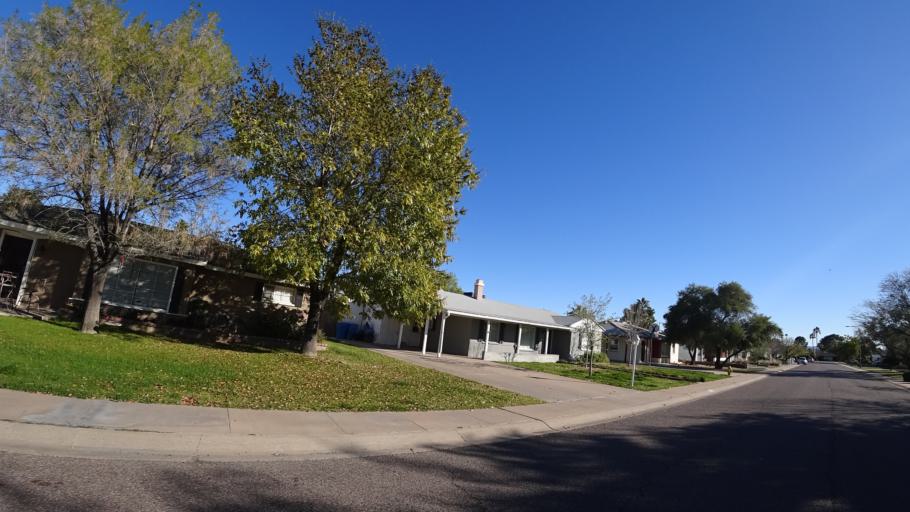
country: US
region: Arizona
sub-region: Maricopa County
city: Phoenix
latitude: 33.5222
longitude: -112.0546
